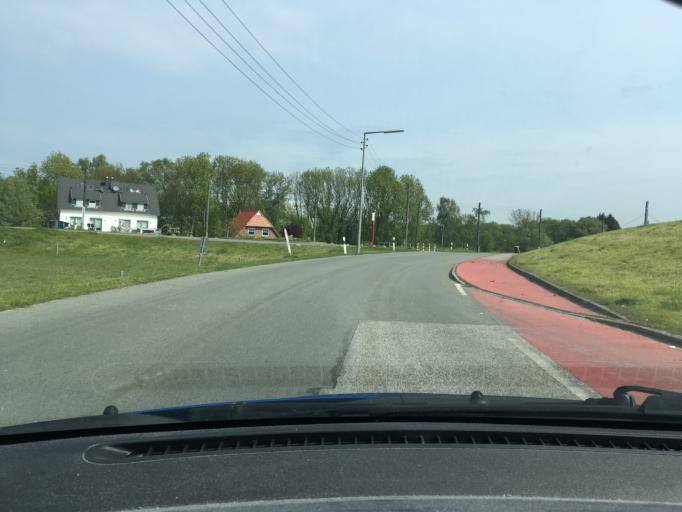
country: DE
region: Hamburg
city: Rothenburgsort
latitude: 53.5034
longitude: 10.0513
